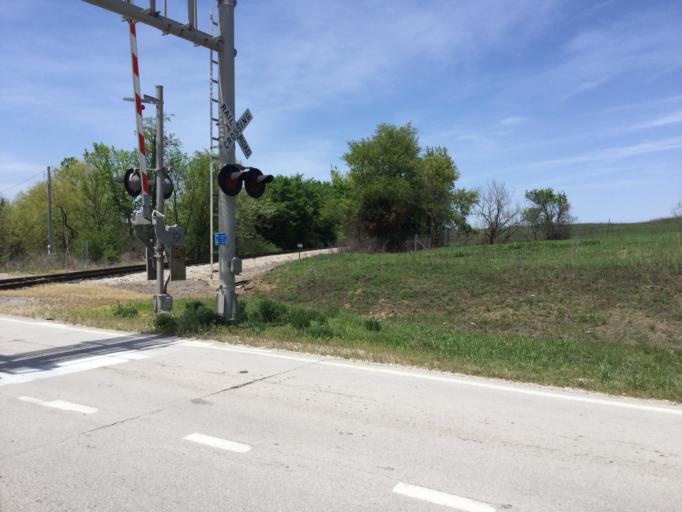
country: US
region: Kansas
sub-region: Montgomery County
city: Cherryvale
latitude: 37.3481
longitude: -95.5942
